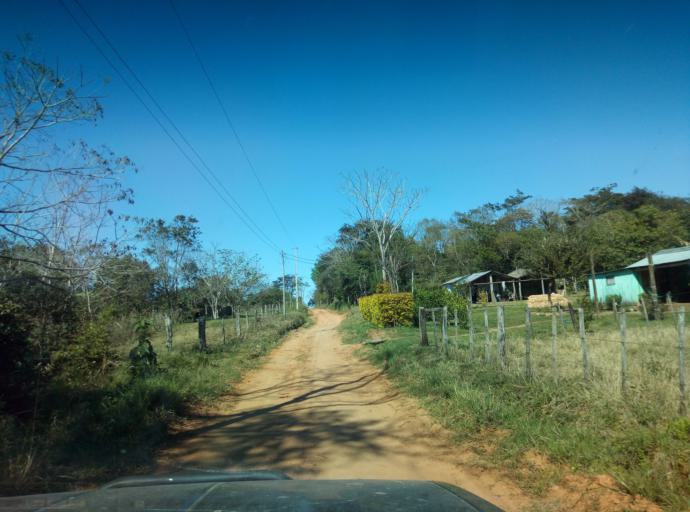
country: PY
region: Caaguazu
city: Doctor Cecilio Baez
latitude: -25.1763
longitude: -56.2020
